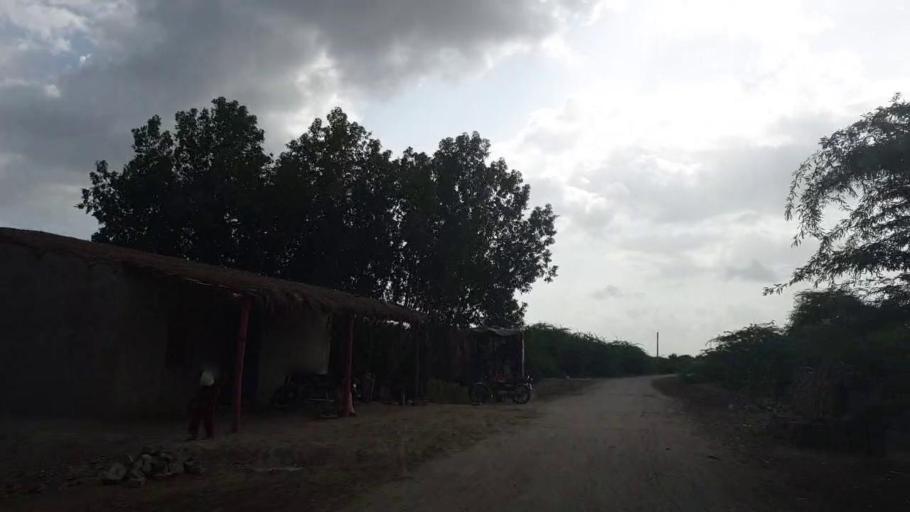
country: PK
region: Sindh
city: Kadhan
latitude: 24.5498
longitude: 69.0633
